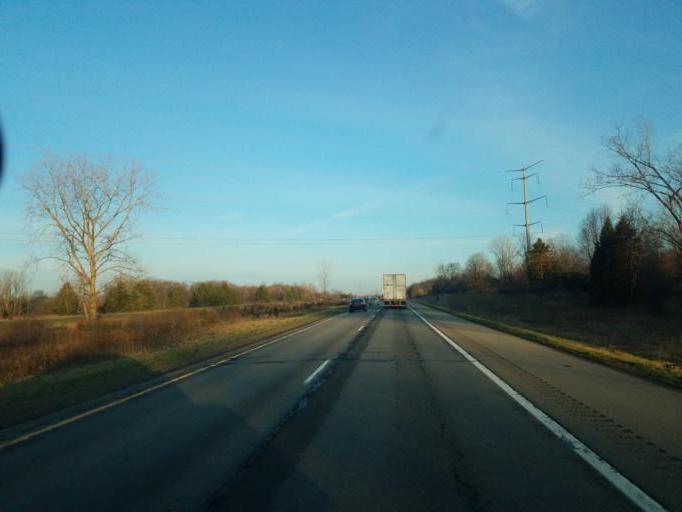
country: US
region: Michigan
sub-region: Livingston County
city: Fowlerville
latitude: 42.6410
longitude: -84.0365
